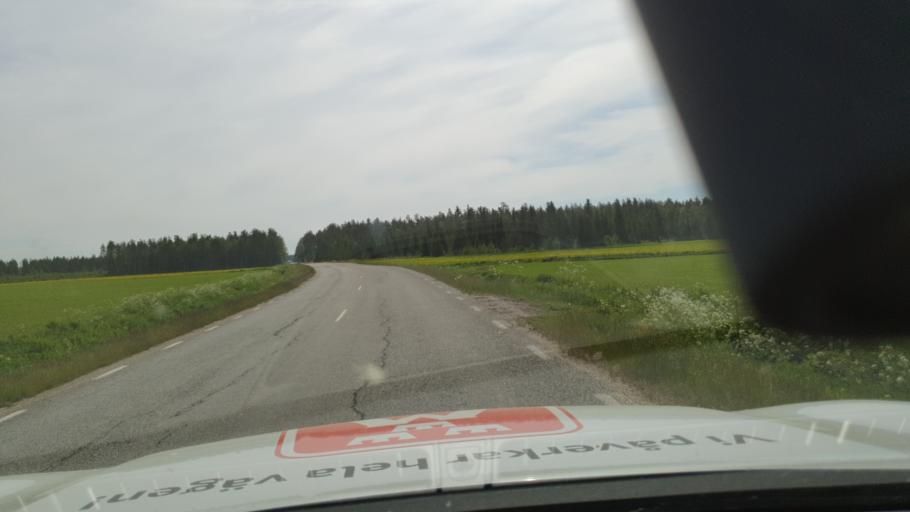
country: SE
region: Vaesterbotten
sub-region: Robertsfors Kommun
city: Robertsfors
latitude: 64.2945
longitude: 20.8931
